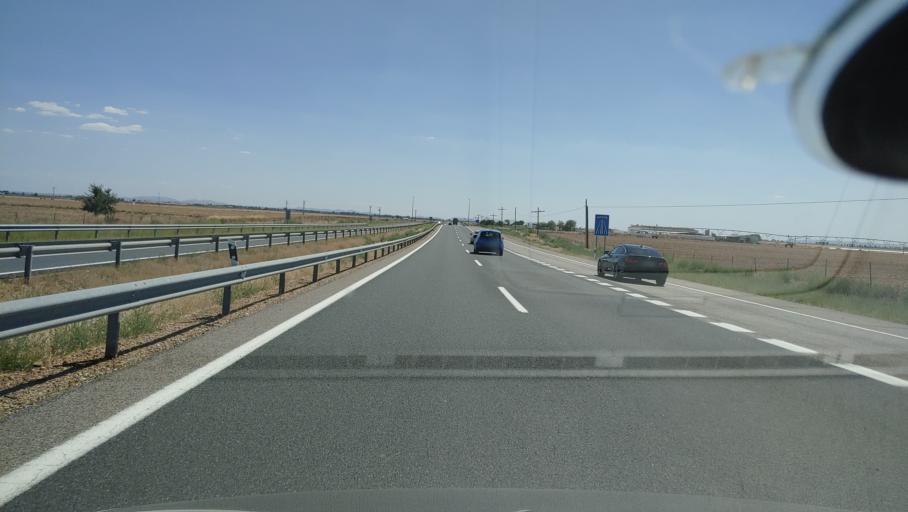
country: ES
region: Castille-La Mancha
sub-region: Provincia de Ciudad Real
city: Villarta de San Juan
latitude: 39.1626
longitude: -3.3912
